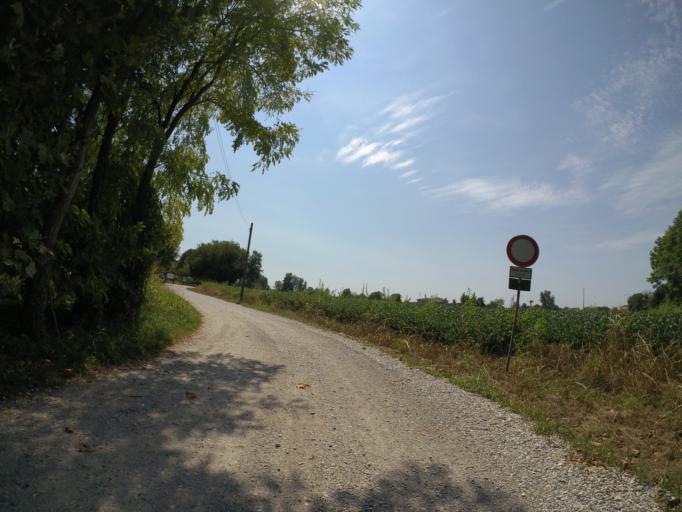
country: IT
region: Friuli Venezia Giulia
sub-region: Provincia di Udine
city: Codroipo
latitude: 45.9551
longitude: 12.9784
